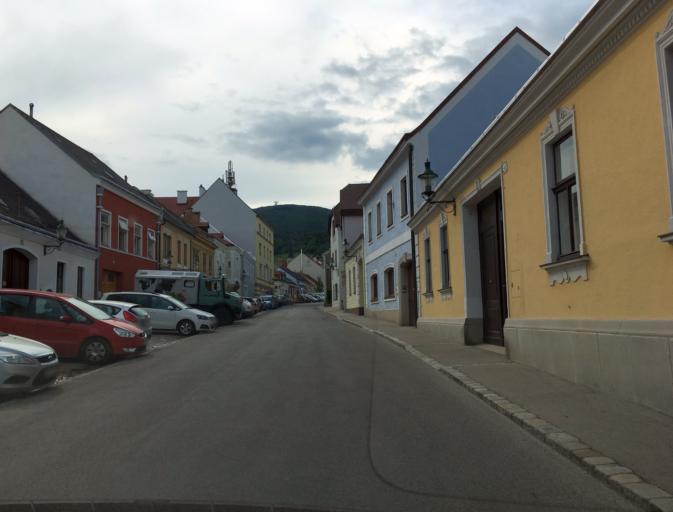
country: AT
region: Lower Austria
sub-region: Politischer Bezirk Modling
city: Gumpoldskirchen
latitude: 48.0439
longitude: 16.2805
